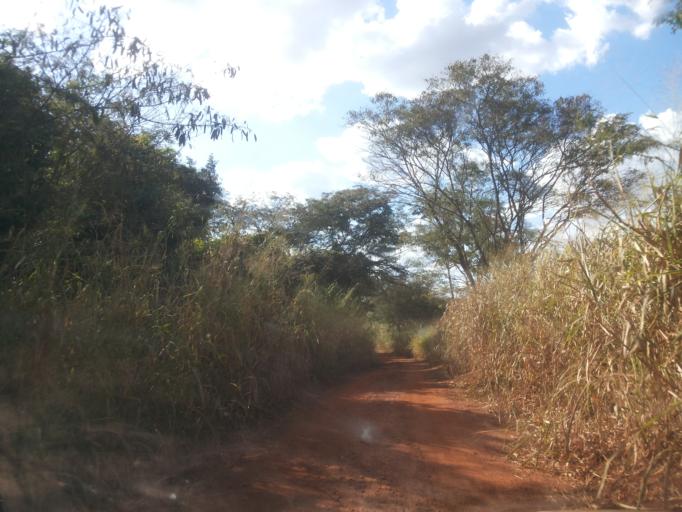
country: BR
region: Minas Gerais
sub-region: Capinopolis
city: Capinopolis
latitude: -18.5956
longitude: -49.4952
